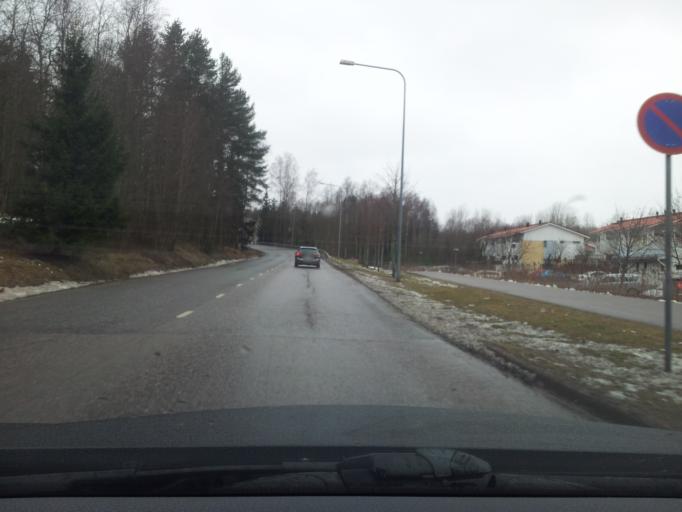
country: FI
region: Uusimaa
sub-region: Helsinki
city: Espoo
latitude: 60.1715
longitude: 24.6801
